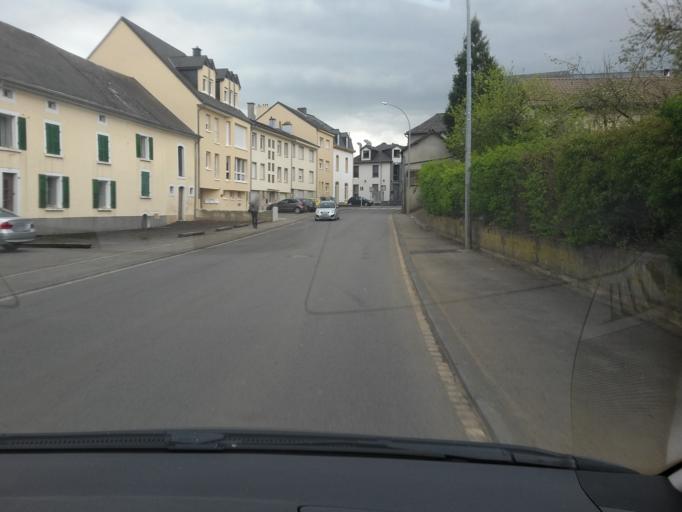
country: LU
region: Luxembourg
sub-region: Canton de Capellen
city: Clemency
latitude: 49.5956
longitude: 5.8772
